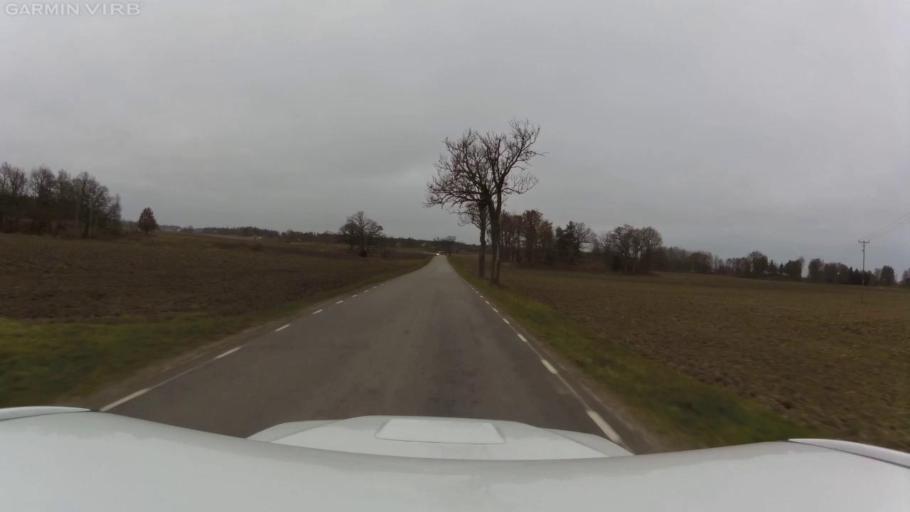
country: SE
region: OEstergoetland
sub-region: Linkopings Kommun
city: Vikingstad
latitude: 58.3717
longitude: 15.4332
